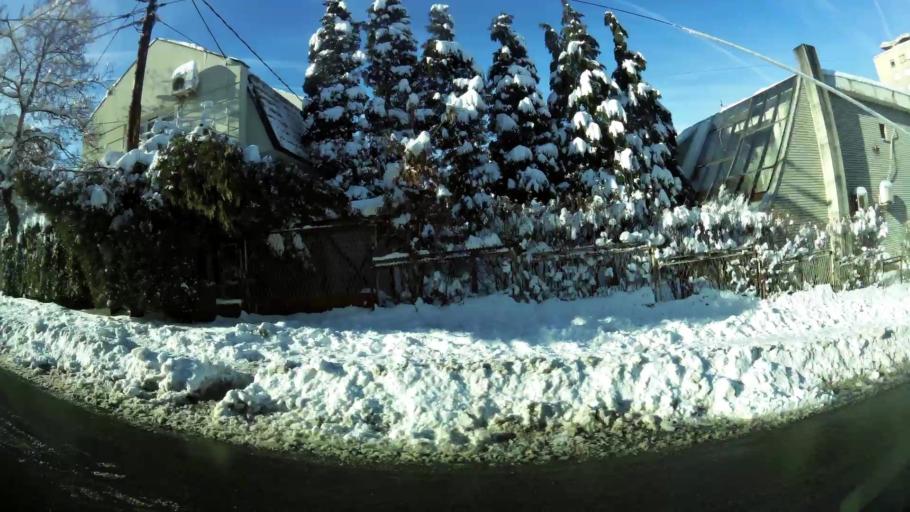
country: RS
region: Central Serbia
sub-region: Belgrade
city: Zvezdara
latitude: 44.7854
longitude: 20.5065
